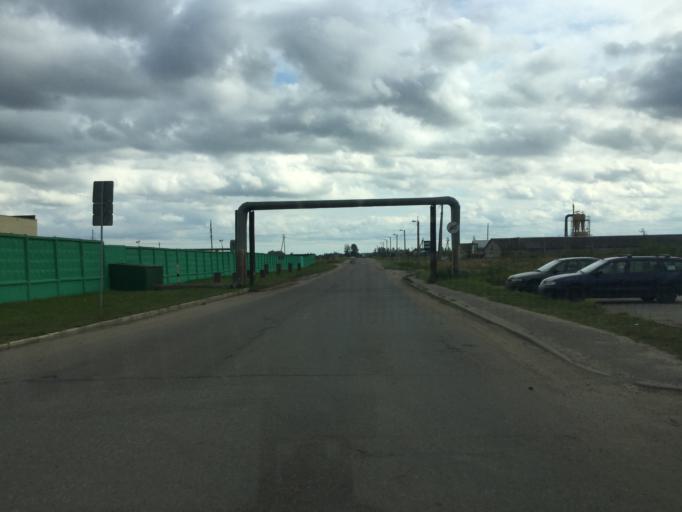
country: BY
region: Vitebsk
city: Vitebsk
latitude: 55.1593
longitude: 30.2635
